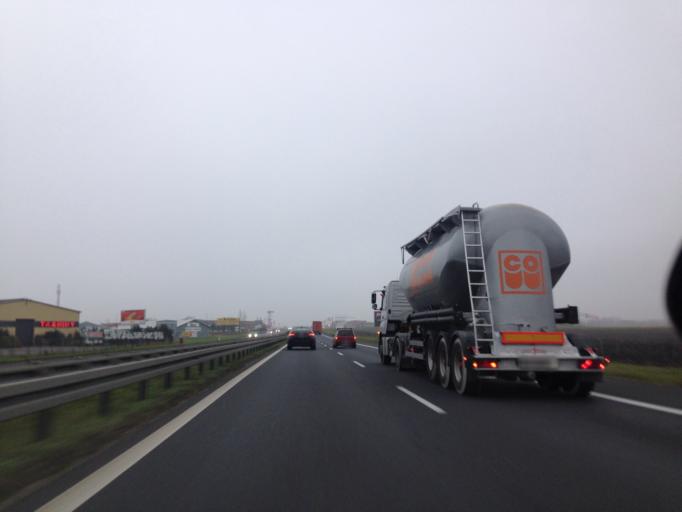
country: PL
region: Lodz Voivodeship
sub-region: Powiat lodzki wschodni
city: Rzgow
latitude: 51.6543
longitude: 19.4819
